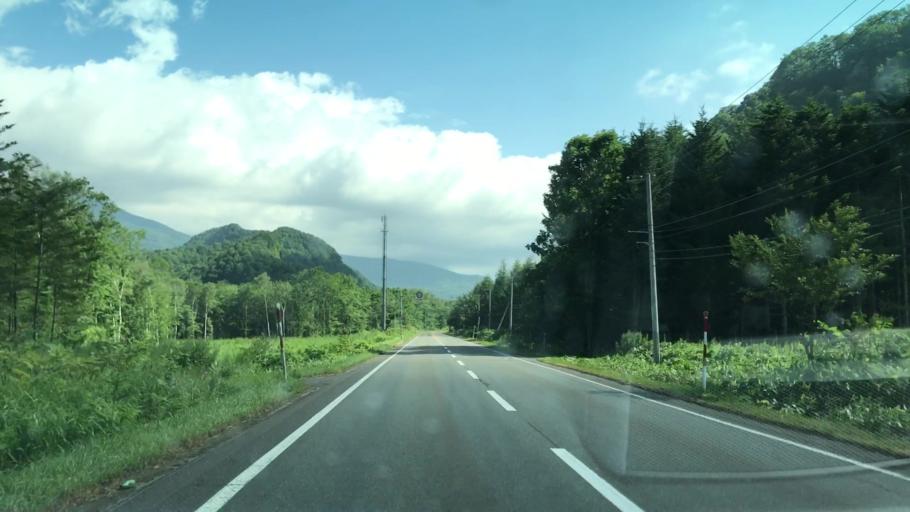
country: JP
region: Hokkaido
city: Shimo-furano
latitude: 42.8466
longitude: 142.4171
